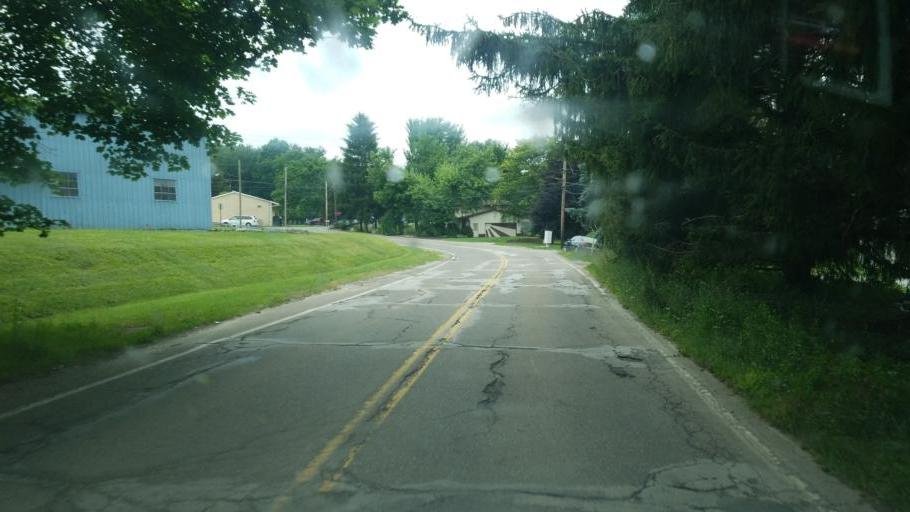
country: US
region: Ohio
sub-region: Summit County
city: Sawyerwood
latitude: 41.0560
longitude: -81.4236
